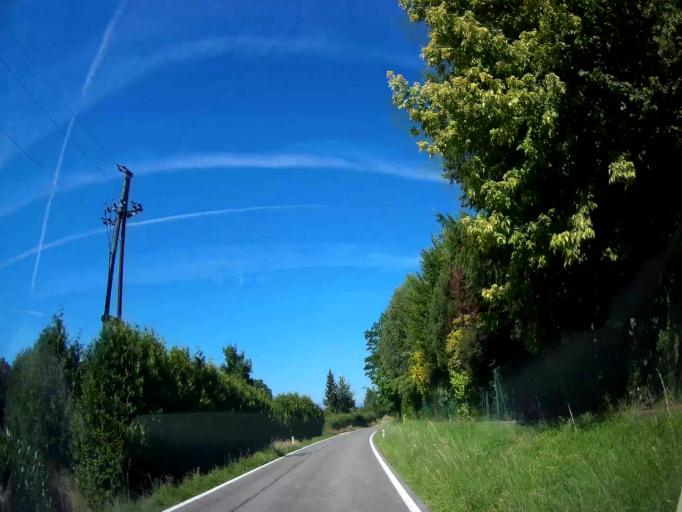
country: AT
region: Carinthia
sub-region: Politischer Bezirk Klagenfurt Land
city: Maria Saal
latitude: 46.6858
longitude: 14.3556
